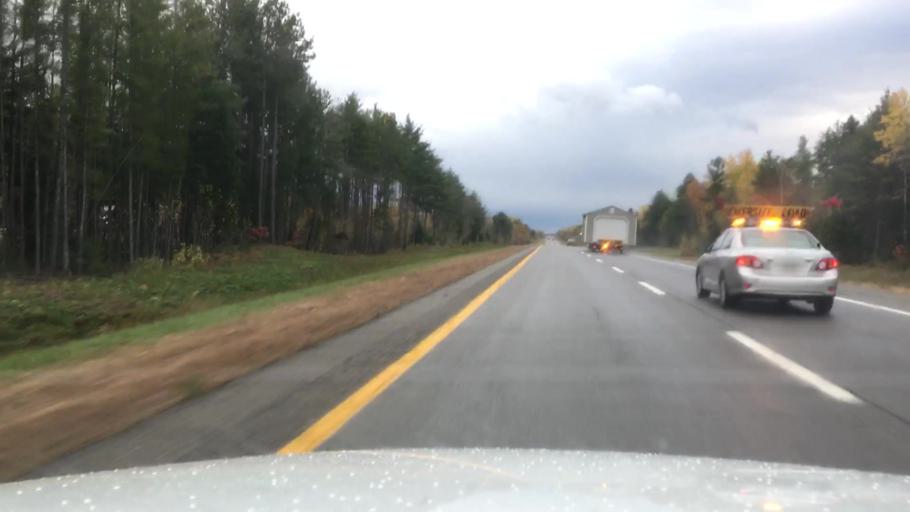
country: US
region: Maine
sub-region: Penobscot County
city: Howland
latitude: 45.2600
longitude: -68.6808
